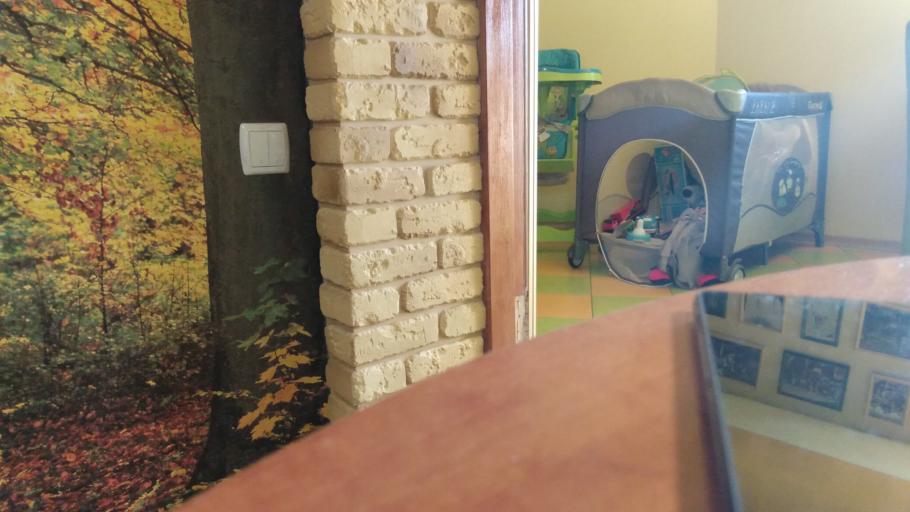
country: RU
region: Tverskaya
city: Bologoye
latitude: 57.9383
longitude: 34.1868
